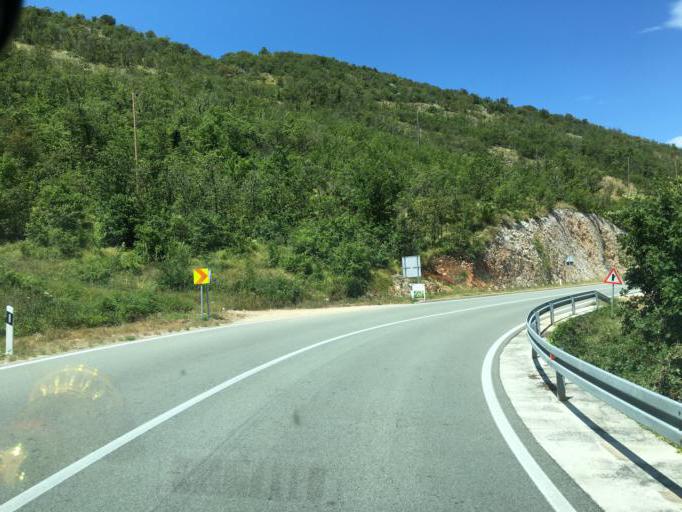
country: HR
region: Istarska
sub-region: Grad Labin
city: Rabac
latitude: 45.1529
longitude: 14.2130
